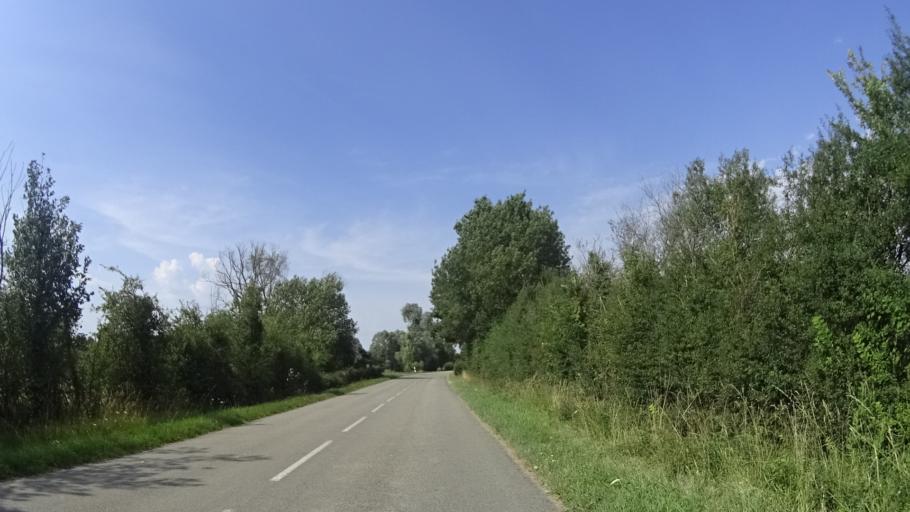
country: FR
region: Pays de la Loire
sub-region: Departement de la Loire-Atlantique
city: Saffre
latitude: 47.4909
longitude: -1.5996
